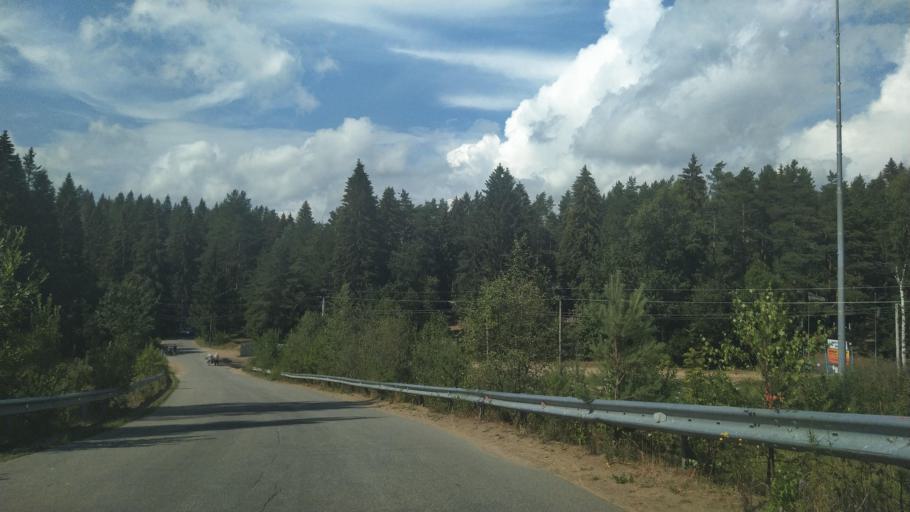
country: RU
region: Leningrad
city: Toksovo
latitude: 60.1677
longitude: 30.5358
